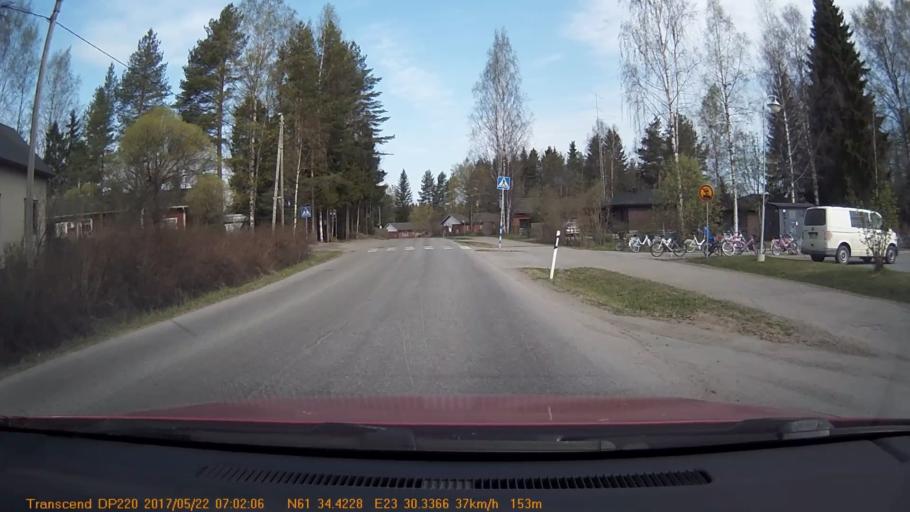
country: FI
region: Pirkanmaa
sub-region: Tampere
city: Yloejaervi
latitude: 61.5737
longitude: 23.5056
